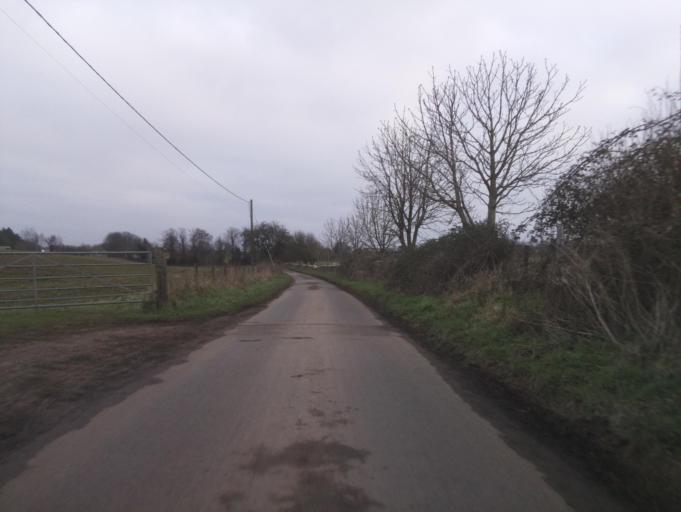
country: GB
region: England
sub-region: Wiltshire
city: Nettleton
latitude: 51.4792
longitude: -2.2842
